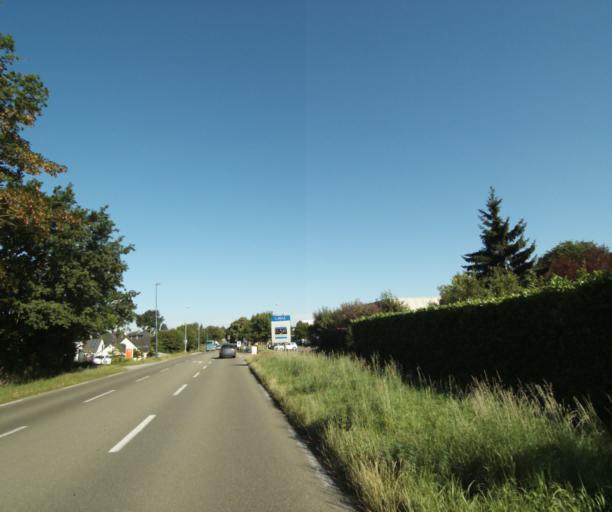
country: FR
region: Pays de la Loire
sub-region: Departement de la Mayenne
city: Laval
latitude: 48.0518
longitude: -0.7383
